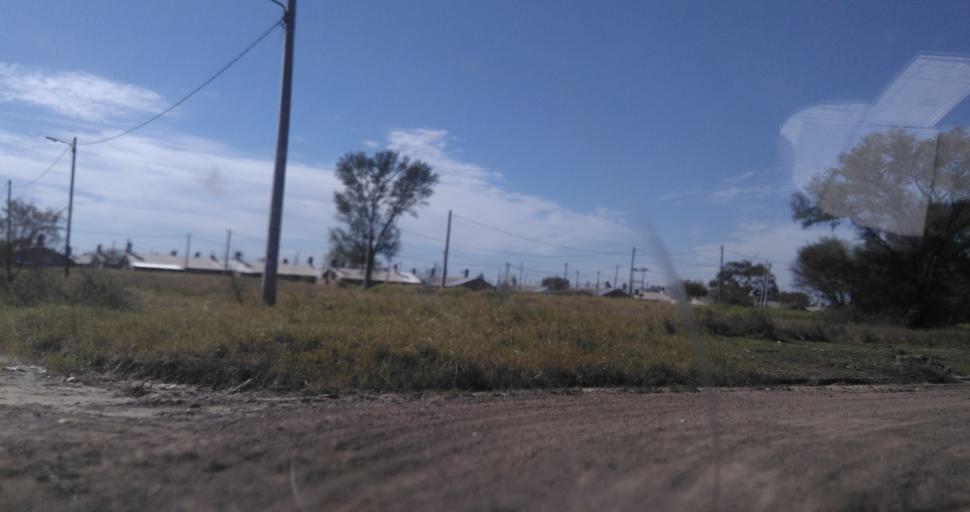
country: AR
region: Chaco
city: Fontana
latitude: -27.4561
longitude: -59.0511
